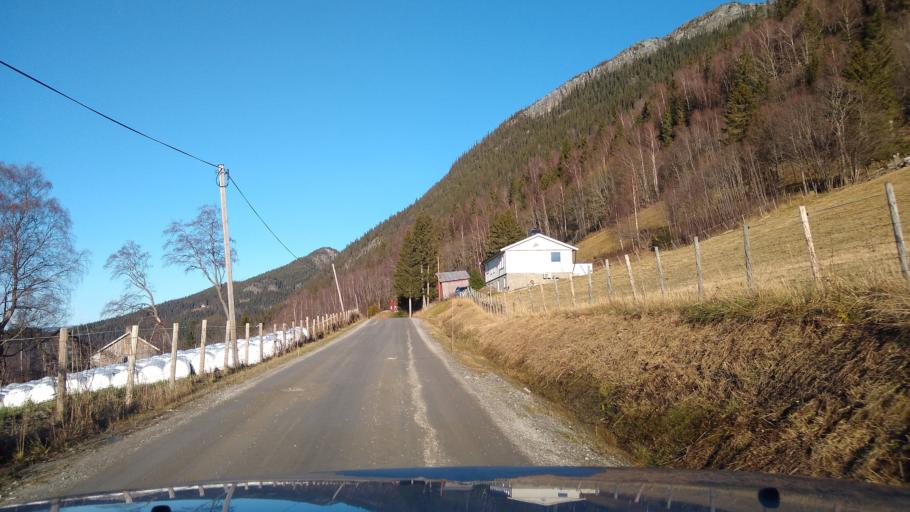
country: NO
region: Oppland
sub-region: Oyer
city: Tretten
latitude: 61.4157
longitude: 10.2399
